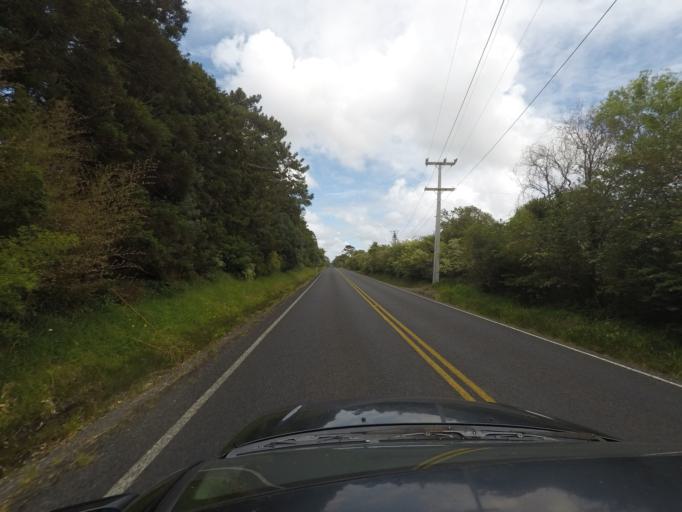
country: NZ
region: Auckland
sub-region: Auckland
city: Parakai
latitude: -36.6441
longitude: 174.5139
